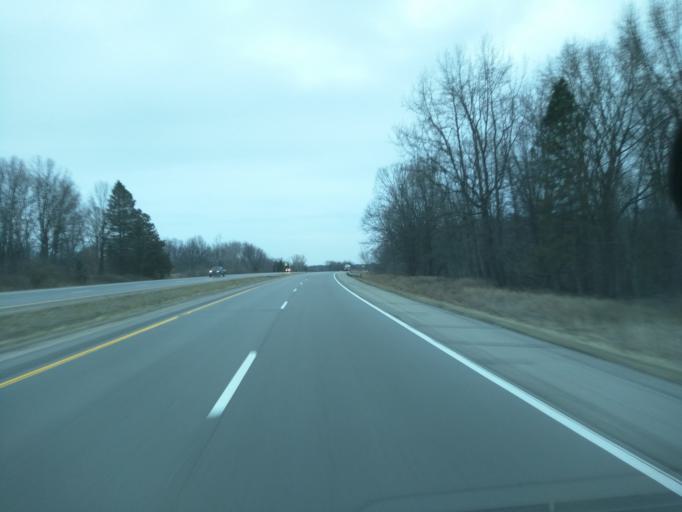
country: US
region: Michigan
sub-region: Ingham County
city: Leslie
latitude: 42.4157
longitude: -84.4297
